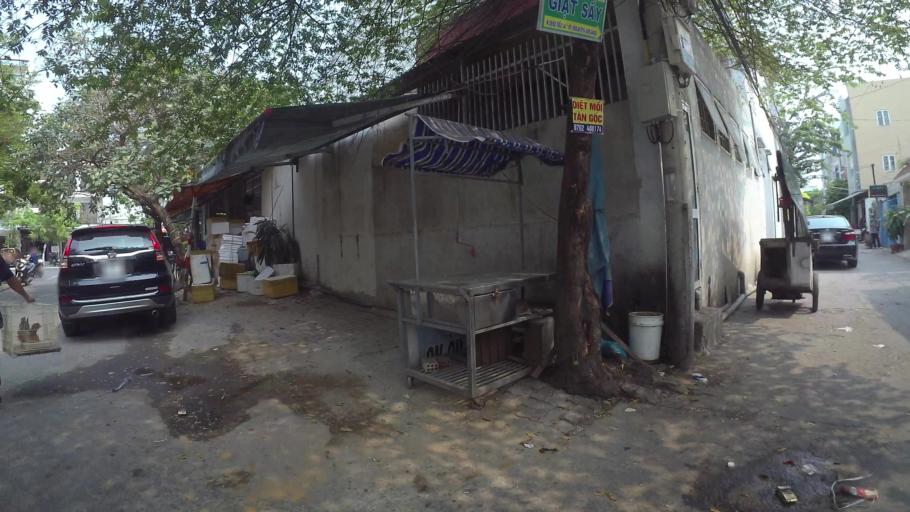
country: VN
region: Da Nang
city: Son Tra
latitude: 16.0420
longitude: 108.2173
